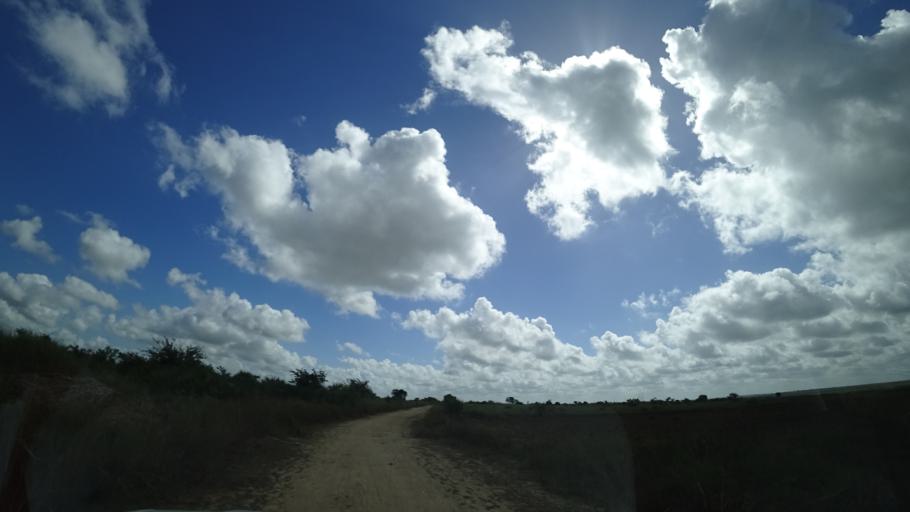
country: MZ
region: Sofala
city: Dondo
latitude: -19.4167
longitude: 34.5656
